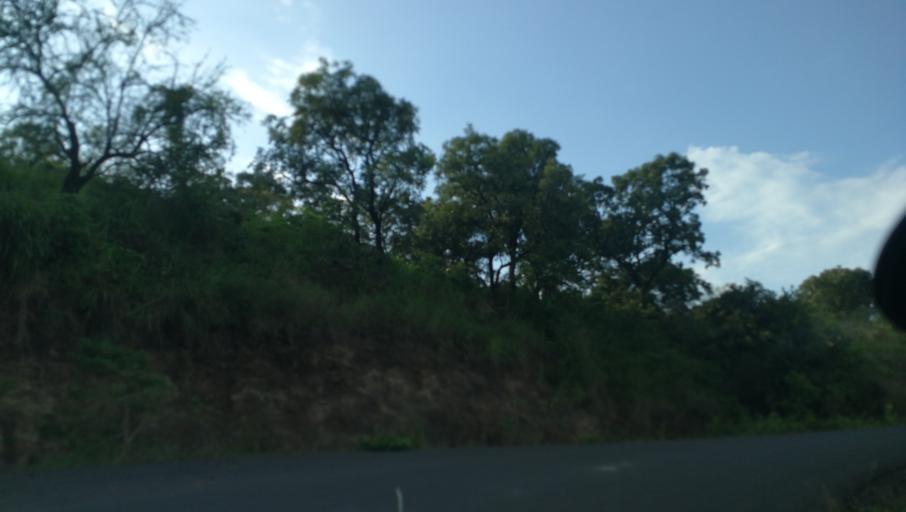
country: ET
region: Southern Nations, Nationalities, and People's Region
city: Areka
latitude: 6.8409
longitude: 37.2756
